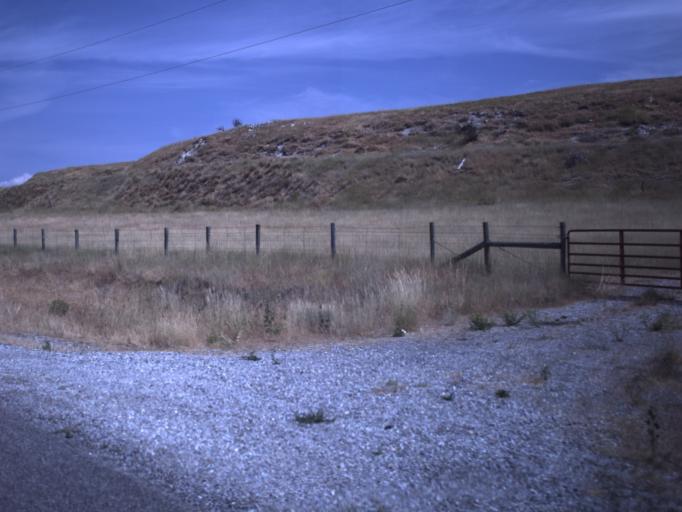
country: US
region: Utah
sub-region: Cache County
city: Mendon
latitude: 41.7953
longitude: -112.0544
